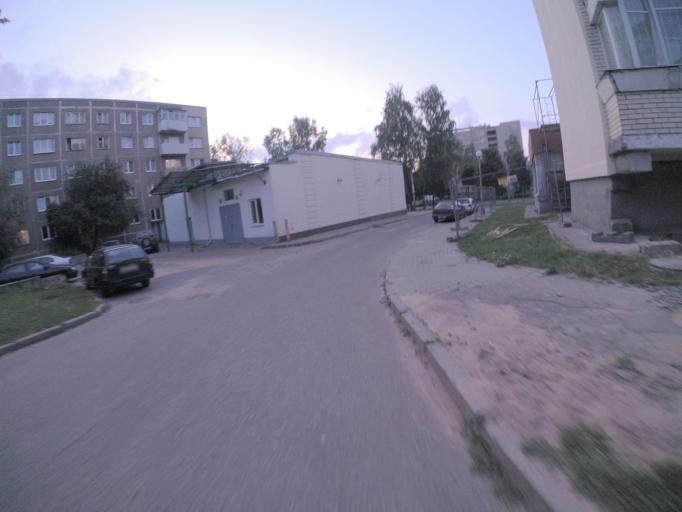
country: BY
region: Grodnenskaya
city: Hrodna
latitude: 53.6984
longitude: 23.8161
